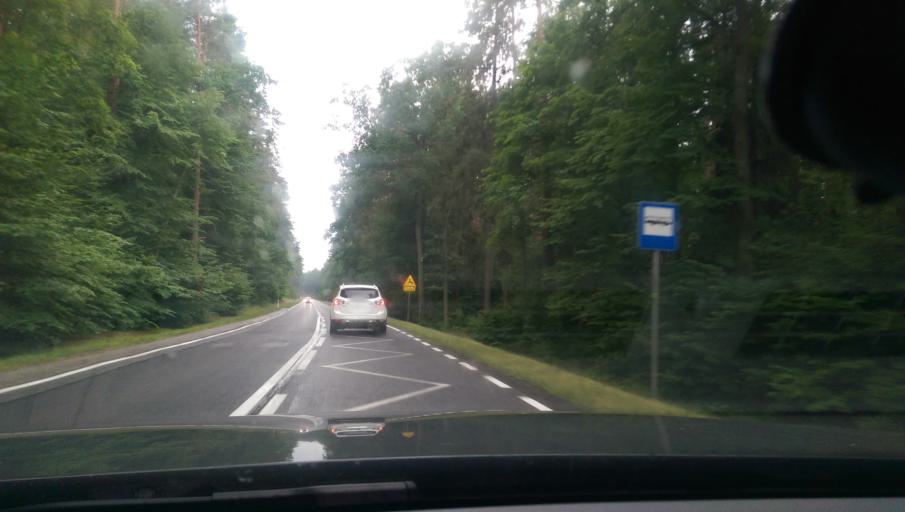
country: PL
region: Warmian-Masurian Voivodeship
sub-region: Powiat szczycienski
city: Szczytno
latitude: 53.5238
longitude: 20.9773
